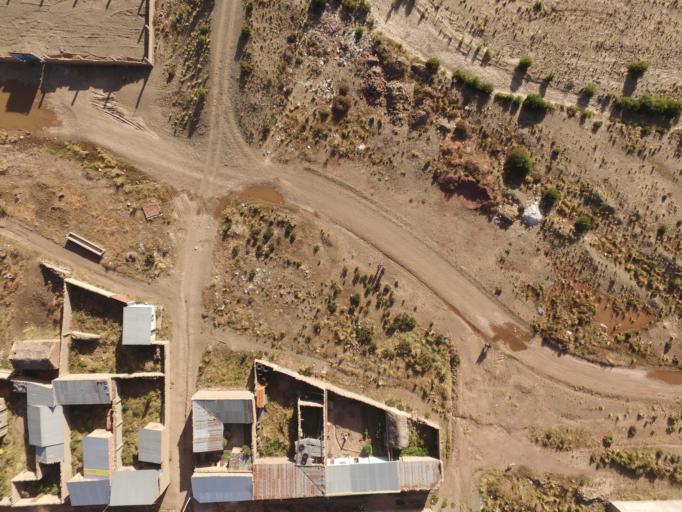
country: BO
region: Oruro
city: Challapata
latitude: -18.6905
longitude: -66.7579
